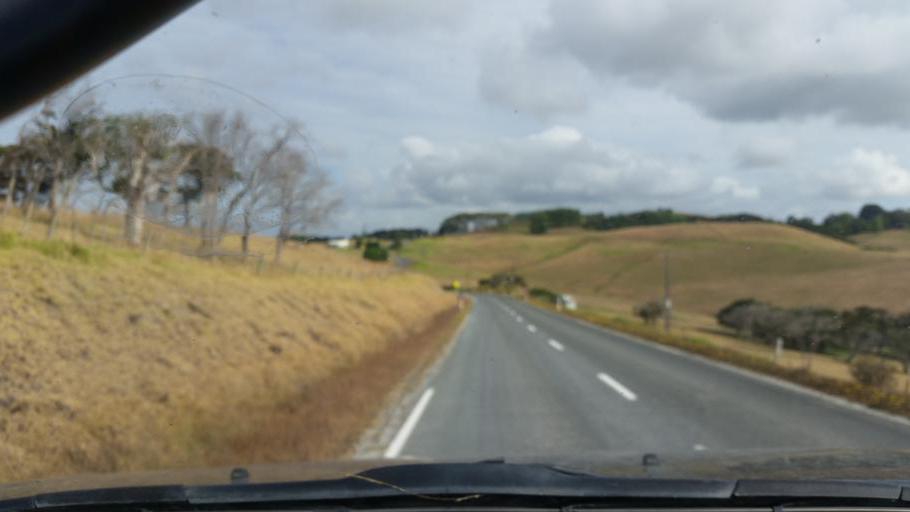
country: NZ
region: Northland
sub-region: Kaipara District
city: Dargaville
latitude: -35.9674
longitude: 173.9348
